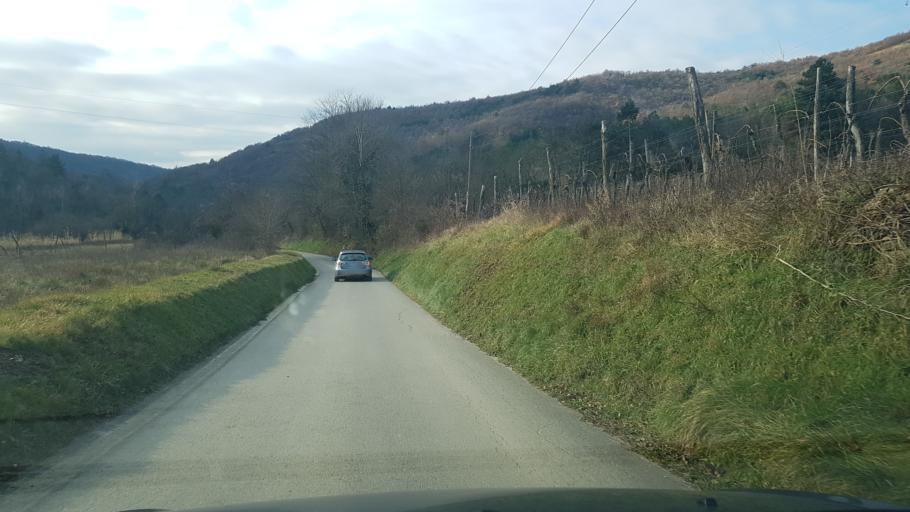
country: SI
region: Koper-Capodistria
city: Prade
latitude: 45.4948
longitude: 13.7806
